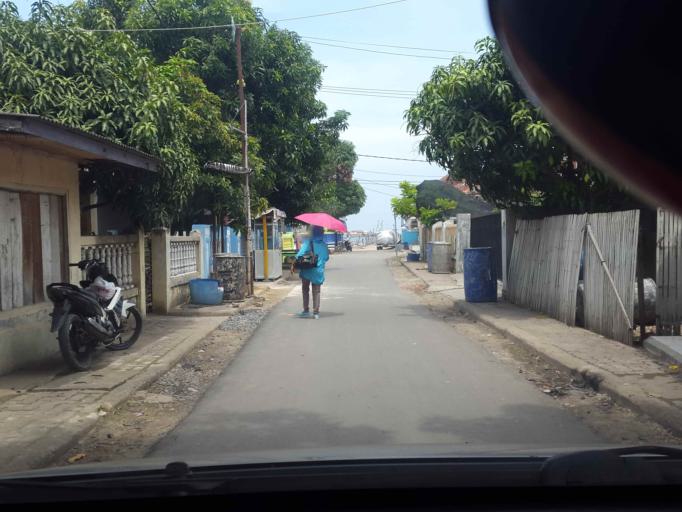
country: ID
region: Lampung
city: Bandarlampung
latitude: -5.4580
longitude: 105.2599
